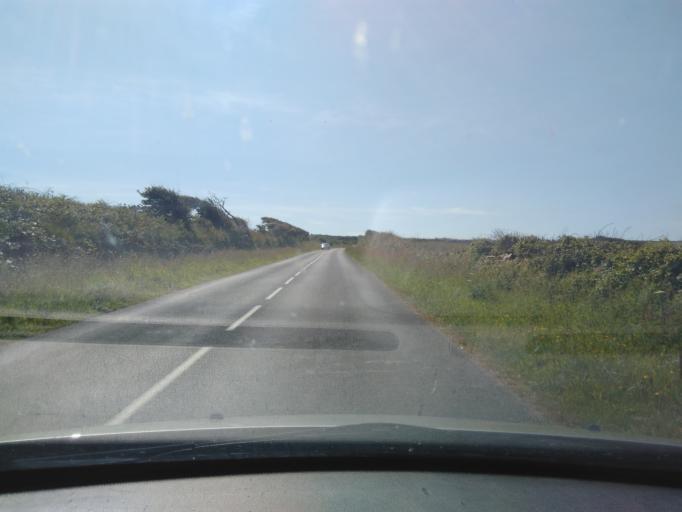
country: FR
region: Lower Normandy
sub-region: Departement de la Manche
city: Beaumont-Hague
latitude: 49.7018
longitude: -1.9285
